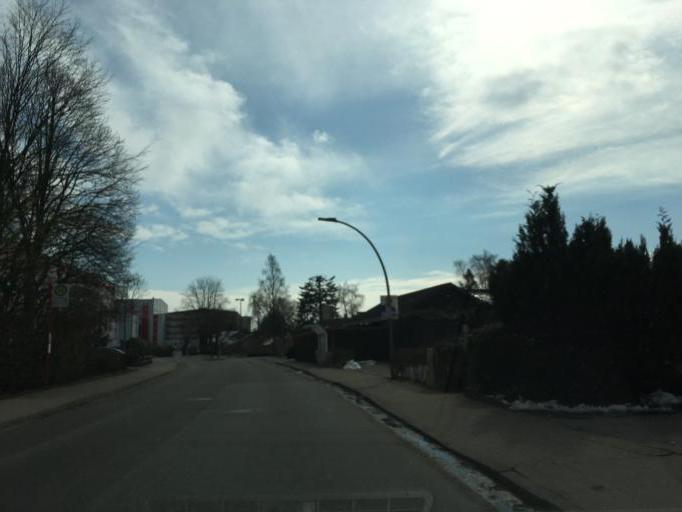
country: DE
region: Schleswig-Holstein
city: Bad Segeberg
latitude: 53.9414
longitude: 10.2949
